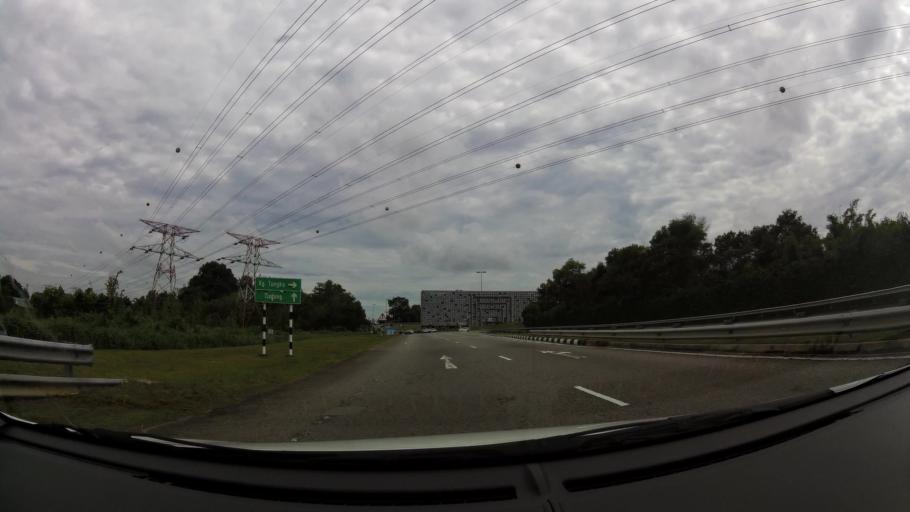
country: BN
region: Brunei and Muara
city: Bandar Seri Begawan
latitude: 4.9153
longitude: 114.9055
